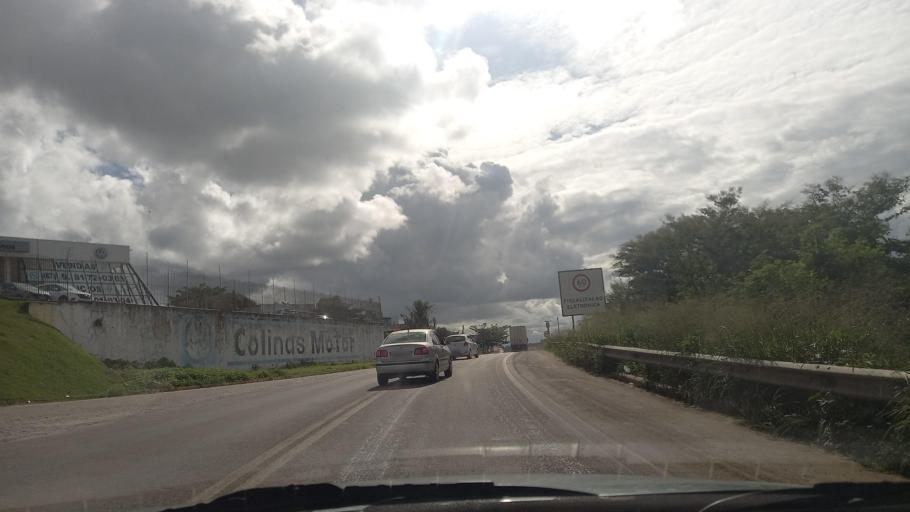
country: BR
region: Pernambuco
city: Garanhuns
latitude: -8.8794
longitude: -36.4797
